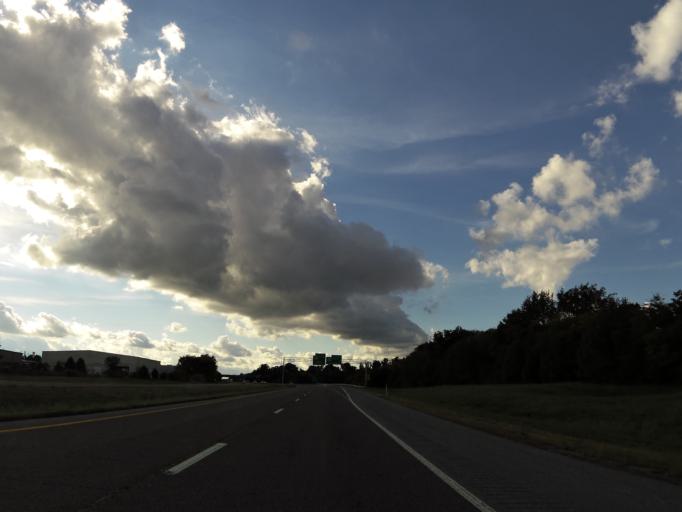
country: US
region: Tennessee
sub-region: Blount County
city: Alcoa
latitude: 35.8326
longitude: -83.9650
